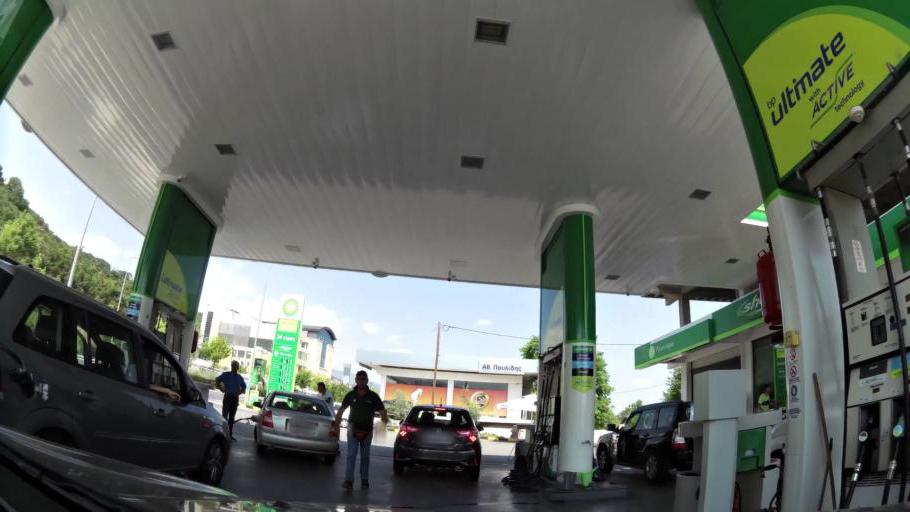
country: GR
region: Central Macedonia
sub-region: Nomos Imathias
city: Veroia
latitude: 40.5072
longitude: 22.2260
